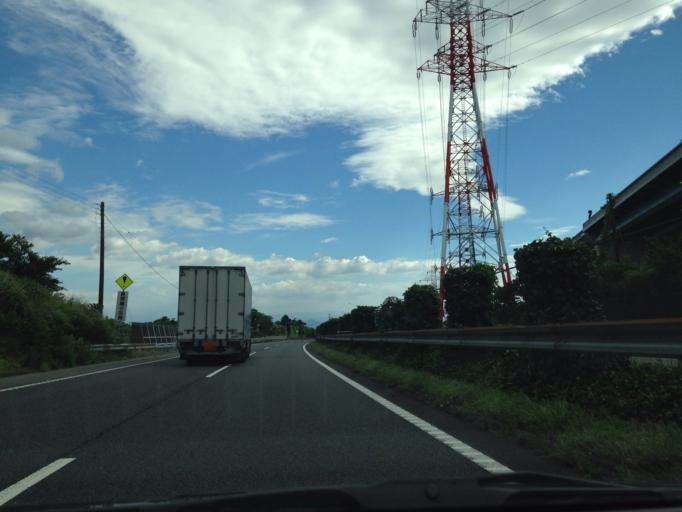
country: JP
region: Shizuoka
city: Gotemba
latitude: 35.2493
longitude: 138.9102
